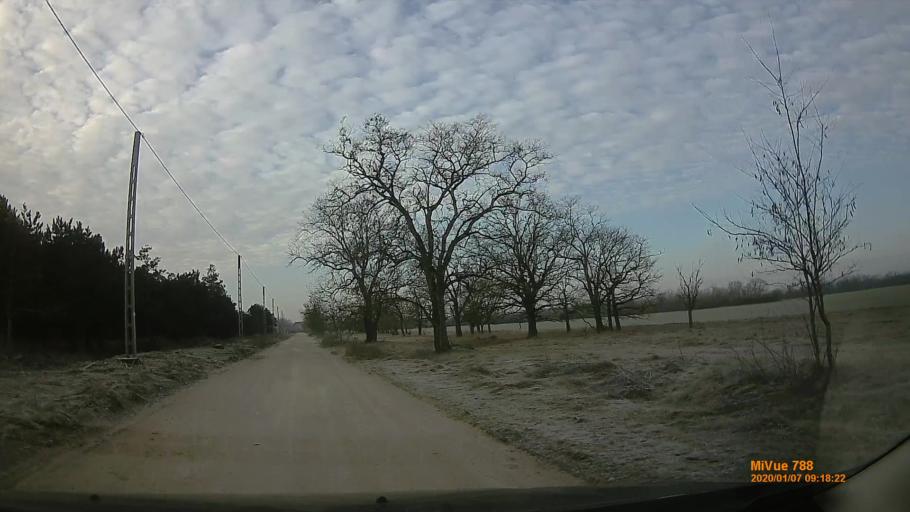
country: HU
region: Gyor-Moson-Sopron
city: Rajka
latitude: 47.9604
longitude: 17.1673
